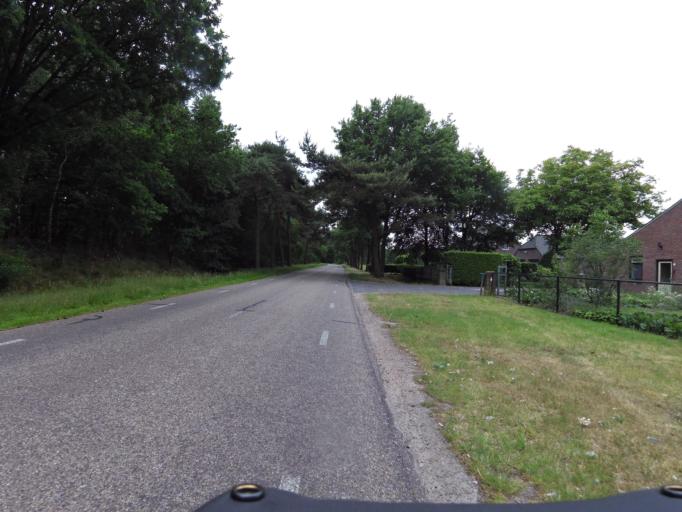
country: NL
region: North Brabant
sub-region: Gemeente Oirschot
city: Middelbeers
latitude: 51.4382
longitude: 5.2102
